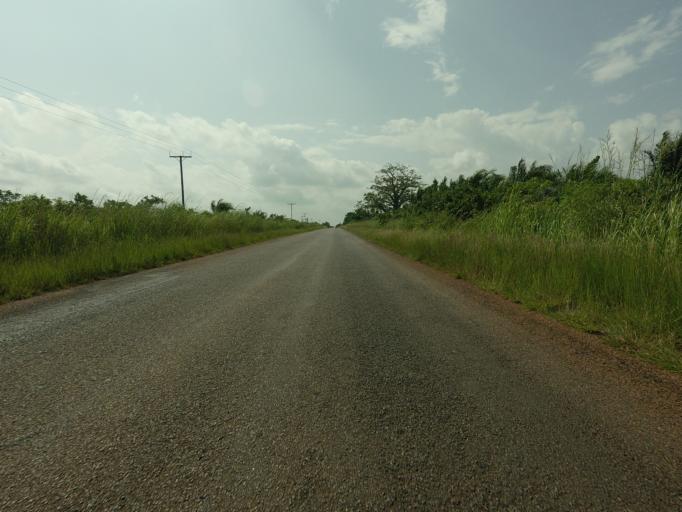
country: TG
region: Maritime
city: Tsevie
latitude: 6.3463
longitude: 0.8722
